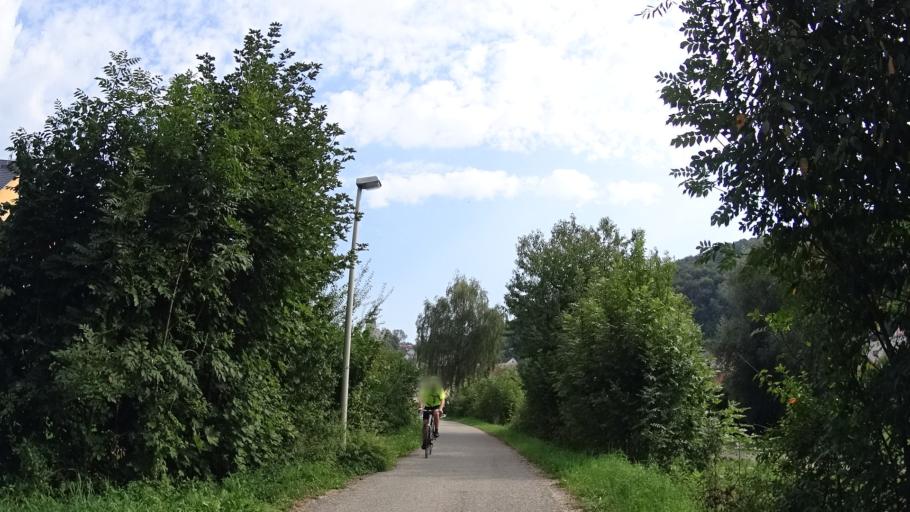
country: DE
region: Bavaria
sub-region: Upper Bavaria
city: Mindelstetten
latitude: 48.8978
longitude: 11.6474
